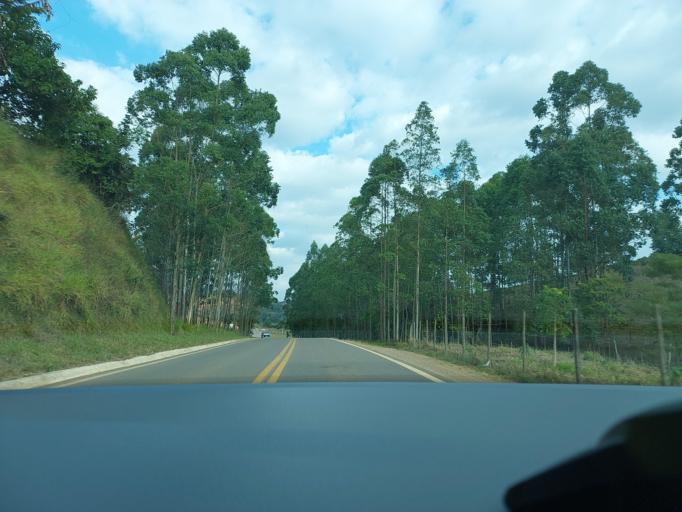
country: BR
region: Minas Gerais
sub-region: Visconde Do Rio Branco
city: Visconde do Rio Branco
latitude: -20.8899
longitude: -42.6580
